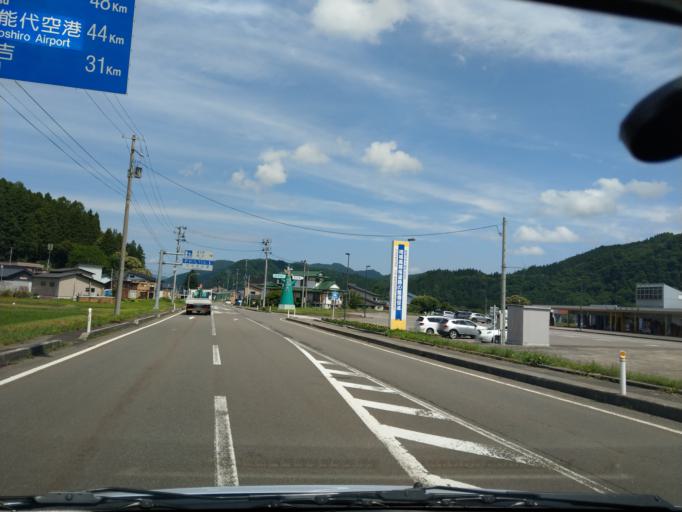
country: JP
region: Akita
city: Kakunodatemachi
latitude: 39.9008
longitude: 140.4572
